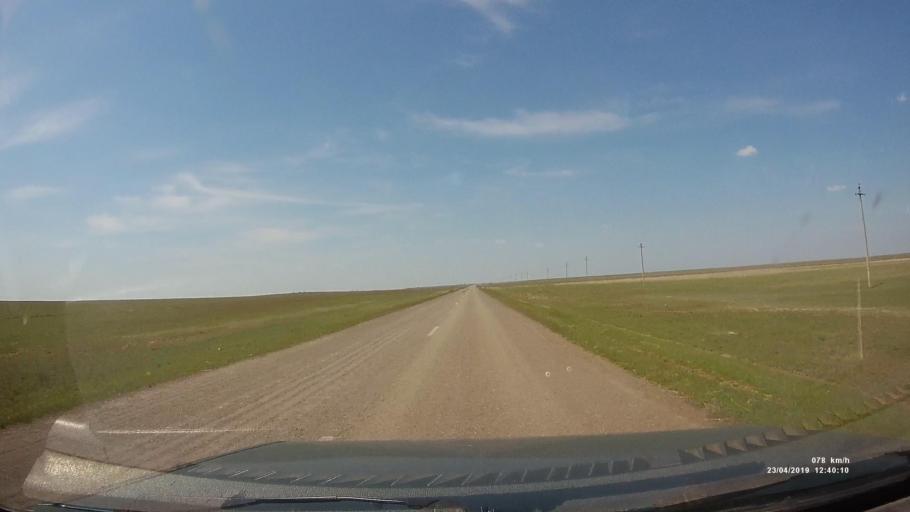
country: RU
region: Kalmykiya
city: Yashalta
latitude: 46.4386
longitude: 42.7001
